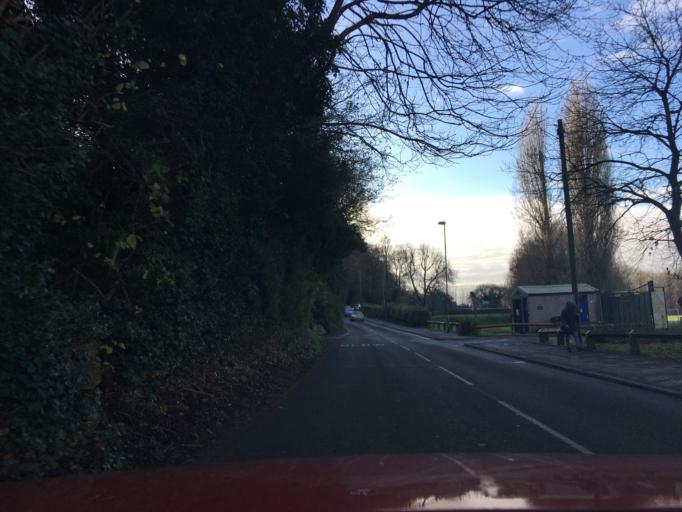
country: GB
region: England
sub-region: Staffordshire
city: Burton upon Trent
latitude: 52.8095
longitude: -1.6161
